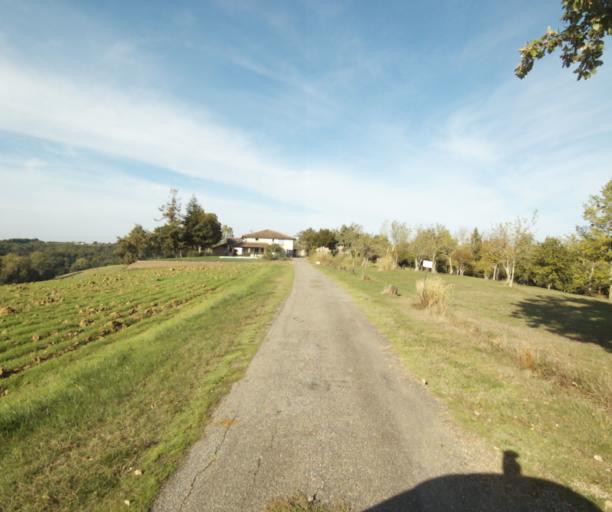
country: FR
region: Midi-Pyrenees
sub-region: Departement du Tarn-et-Garonne
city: Nohic
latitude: 43.9306
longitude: 1.4537
